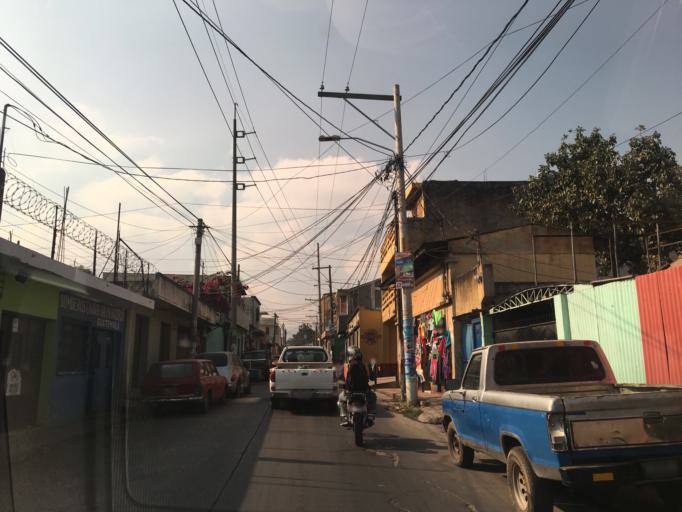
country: GT
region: Guatemala
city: Villa Nueva
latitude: 14.5270
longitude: -90.5845
